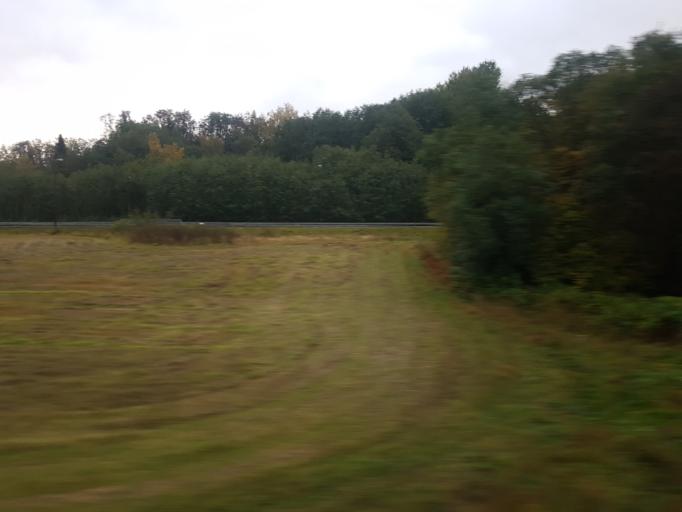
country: NO
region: Sor-Trondelag
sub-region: Melhus
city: Lundamo
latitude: 63.1373
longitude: 10.2594
